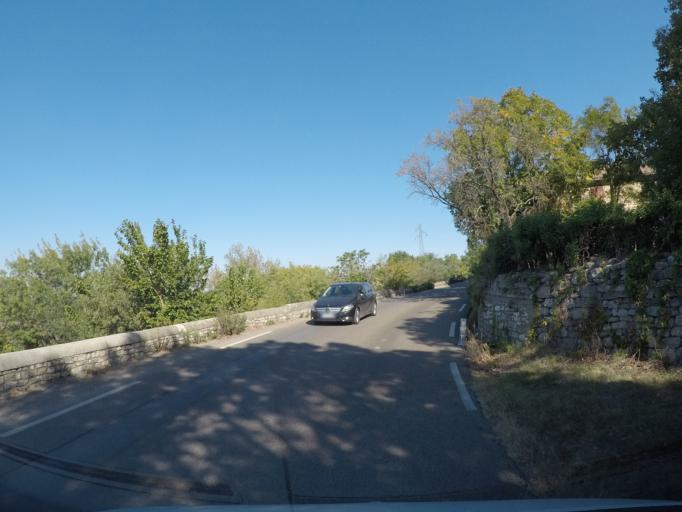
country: FR
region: Languedoc-Roussillon
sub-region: Departement du Gard
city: Uzes
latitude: 44.0075
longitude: 4.4046
